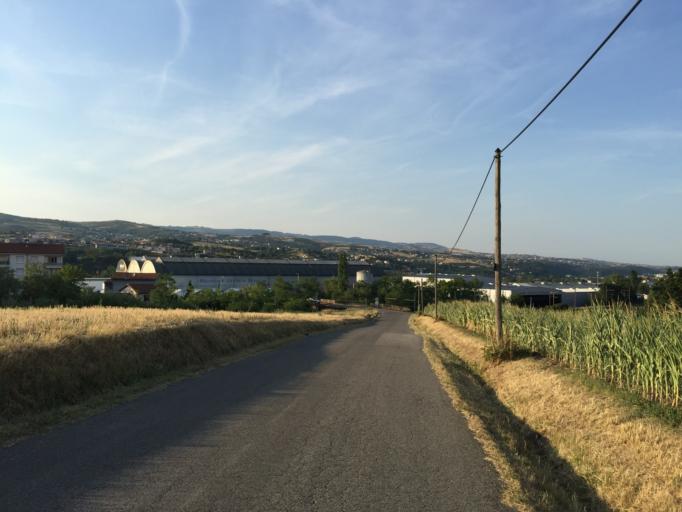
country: FR
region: Rhone-Alpes
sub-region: Departement de la Loire
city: La Grand-Croix
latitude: 45.4832
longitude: 4.5494
